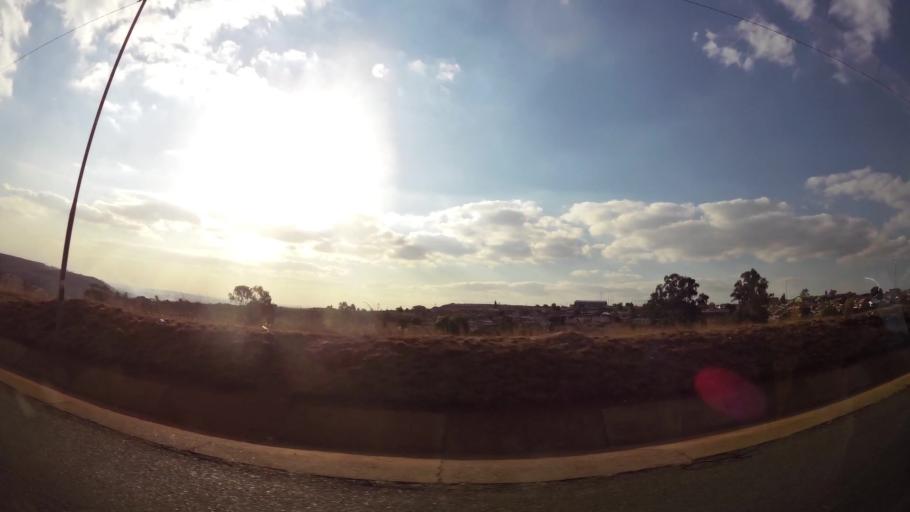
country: ZA
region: Gauteng
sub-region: West Rand District Municipality
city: Krugersdorp
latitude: -26.0845
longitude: 27.7524
